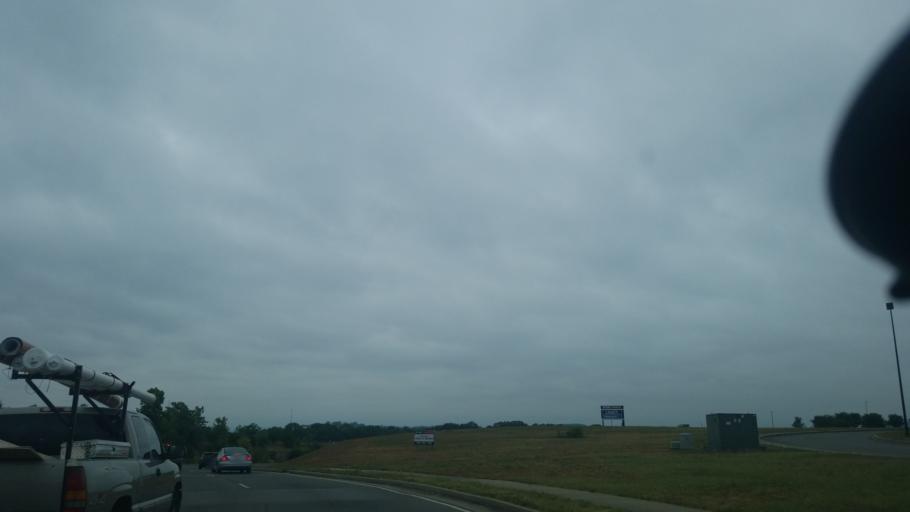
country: US
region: Tennessee
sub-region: Davidson County
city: Nashville
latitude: 36.2437
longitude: -86.7580
